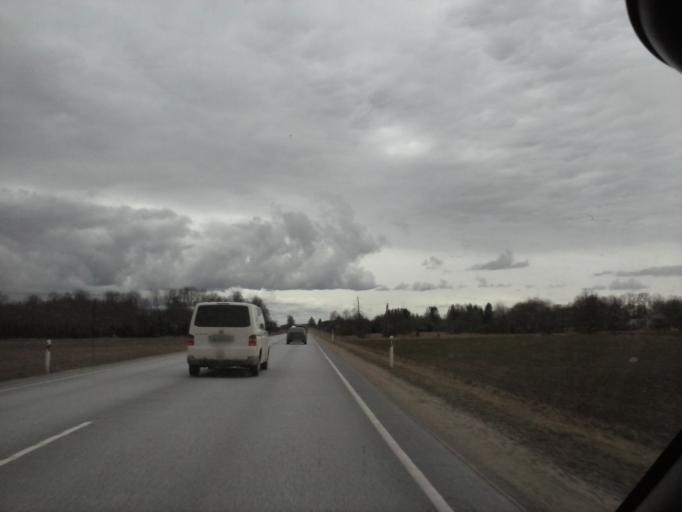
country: EE
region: Jaervamaa
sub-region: Paide linn
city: Paide
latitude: 58.7978
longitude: 25.7580
